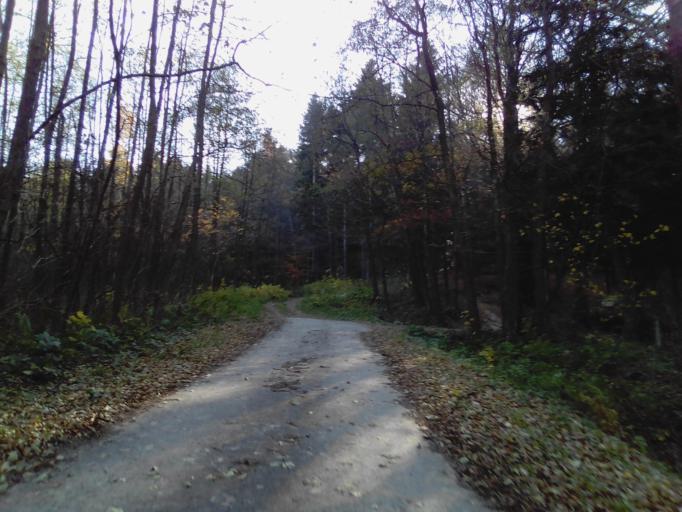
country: PL
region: Subcarpathian Voivodeship
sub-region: Powiat strzyzowski
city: Wisniowa
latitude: 49.8521
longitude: 21.6634
